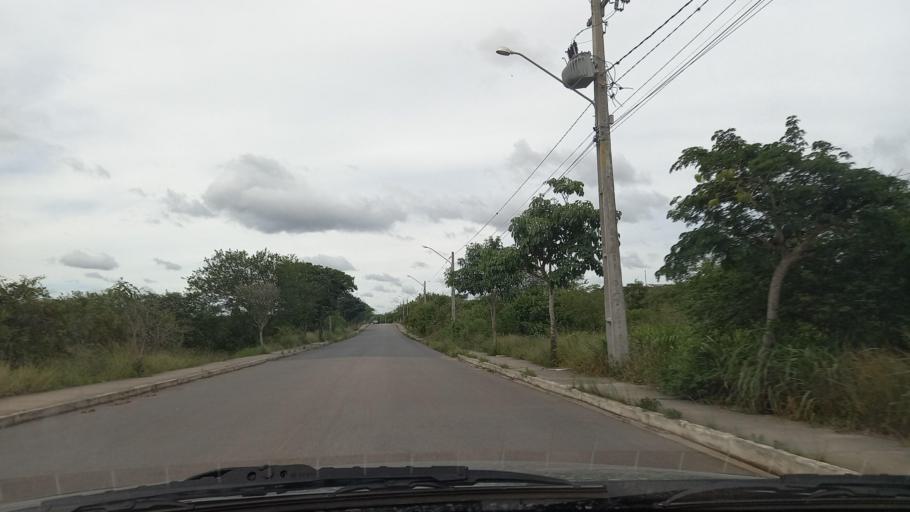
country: BR
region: Pernambuco
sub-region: Gravata
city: Gravata
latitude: -8.2091
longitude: -35.5940
